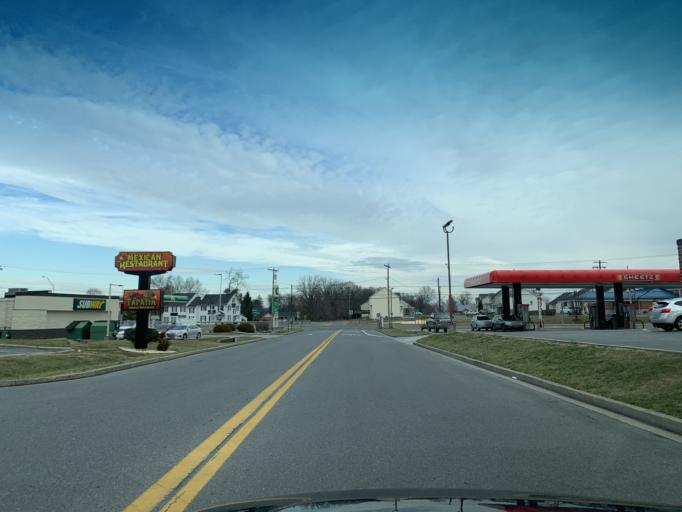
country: US
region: West Virginia
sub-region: Berkeley County
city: Martinsburg
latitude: 39.4631
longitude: -77.9882
